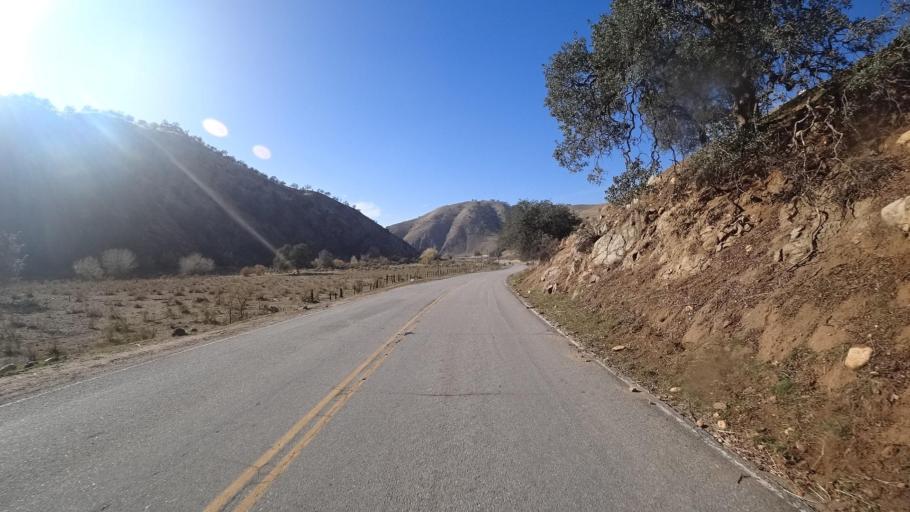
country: US
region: California
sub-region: Kern County
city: Bear Valley Springs
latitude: 35.2991
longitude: -118.5920
